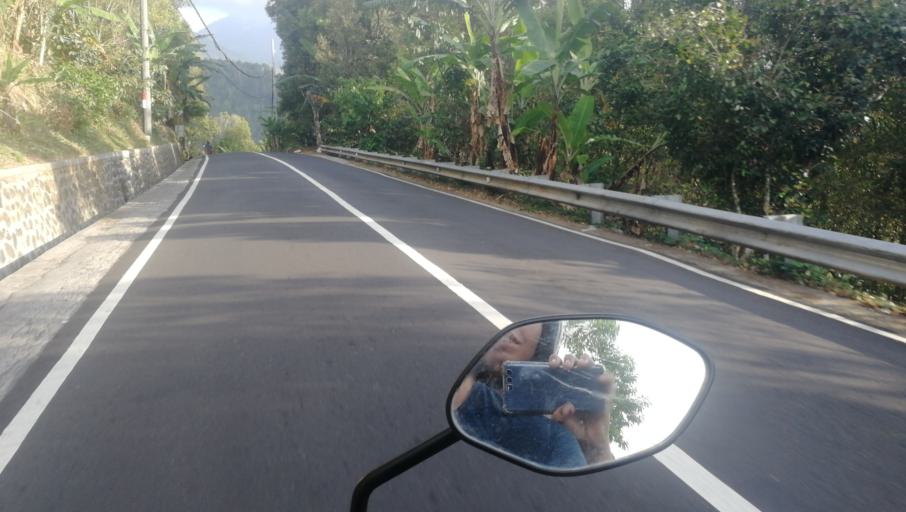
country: ID
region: Bali
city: Munduk
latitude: -8.2601
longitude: 115.0713
